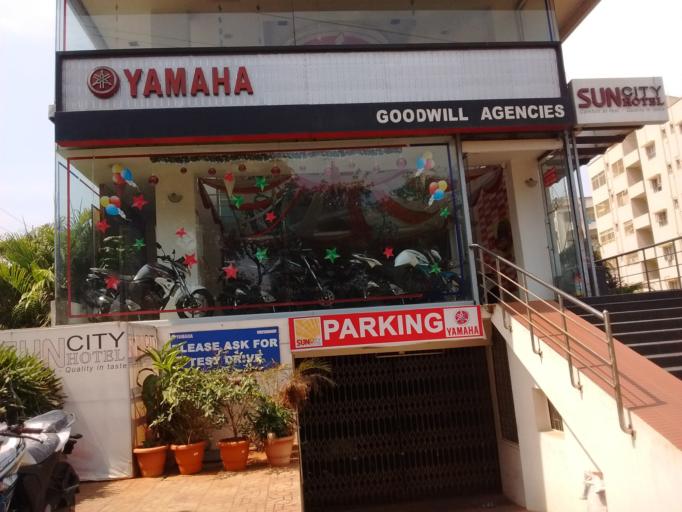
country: IN
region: Andhra Pradesh
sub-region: Krishna
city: Yanamalakuduru
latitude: 16.5146
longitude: 80.6691
